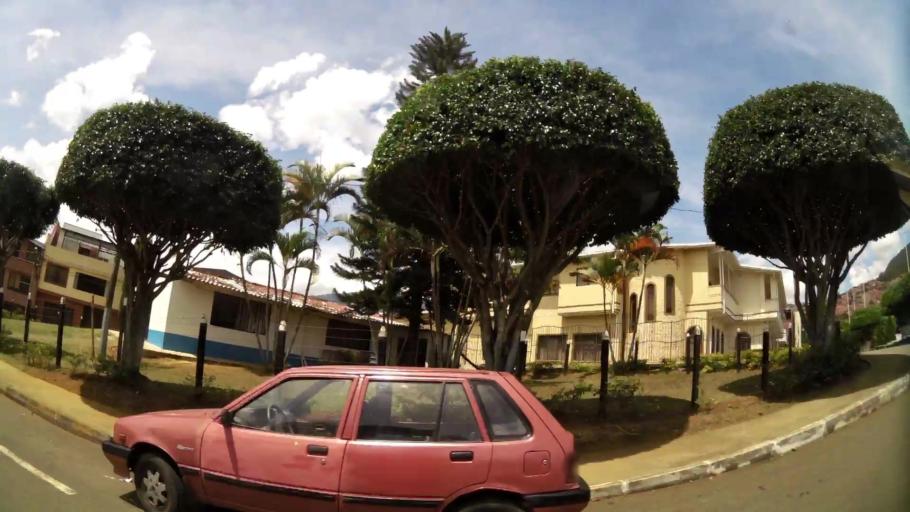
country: CO
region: Antioquia
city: Bello
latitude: 6.3447
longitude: -75.5446
